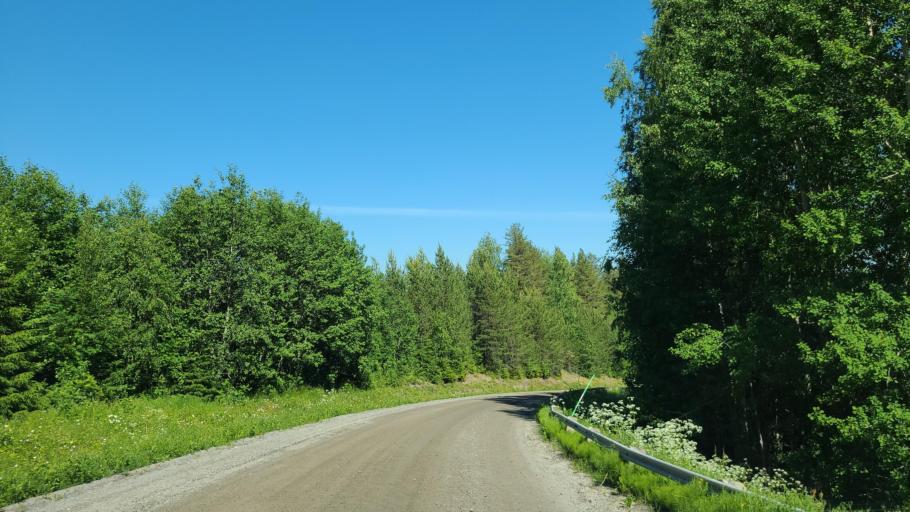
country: SE
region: Vaesterbotten
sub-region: Bjurholms Kommun
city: Bjurholm
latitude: 63.6469
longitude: 19.2260
